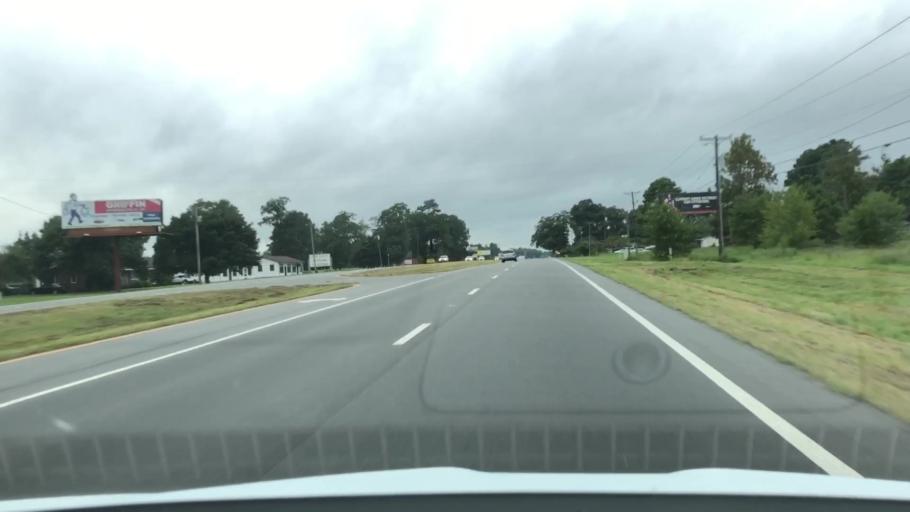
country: US
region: North Carolina
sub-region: Lenoir County
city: La Grange
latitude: 35.2782
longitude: -77.7484
